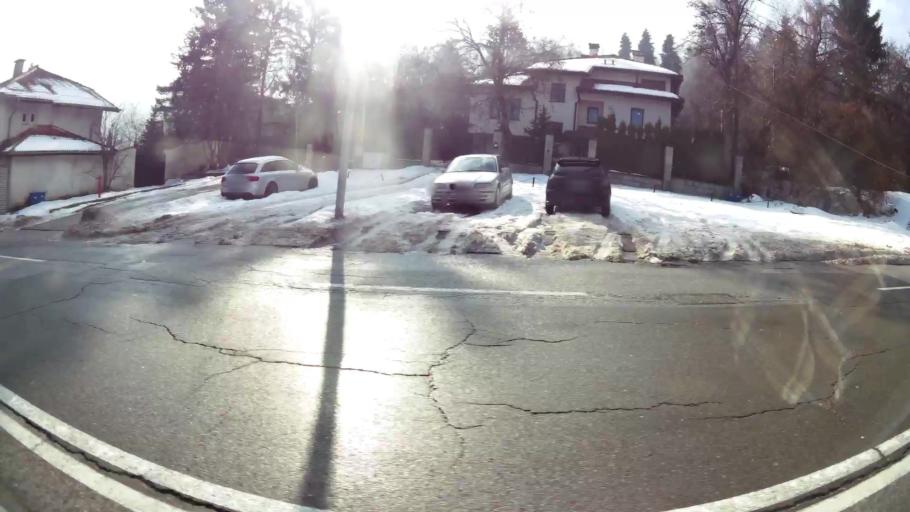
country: BG
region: Sofia-Capital
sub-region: Stolichna Obshtina
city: Sofia
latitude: 42.6489
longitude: 23.2536
